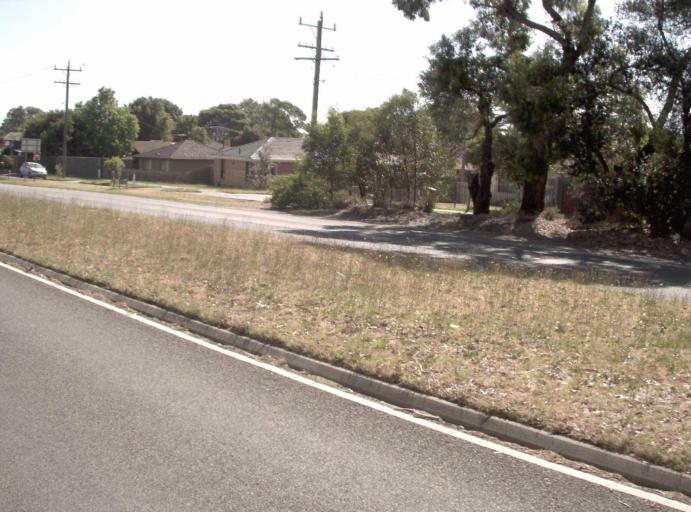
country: AU
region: Victoria
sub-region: Frankston
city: Frankston North
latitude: -38.1214
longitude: 145.1447
